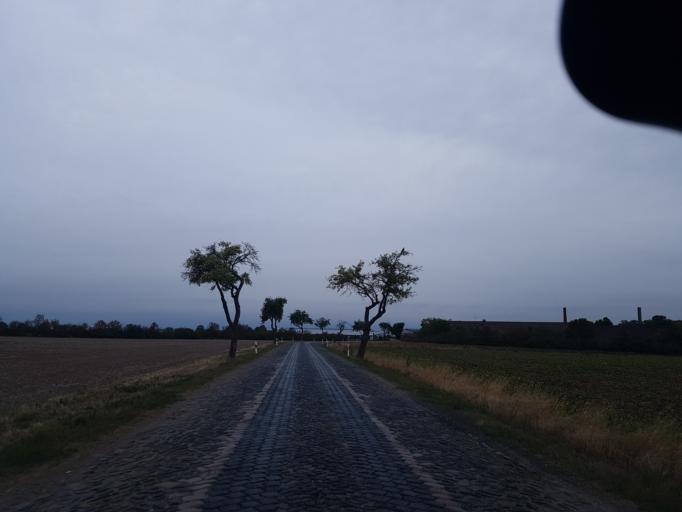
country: DE
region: Saxony
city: Arzberg
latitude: 51.5077
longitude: 13.1621
